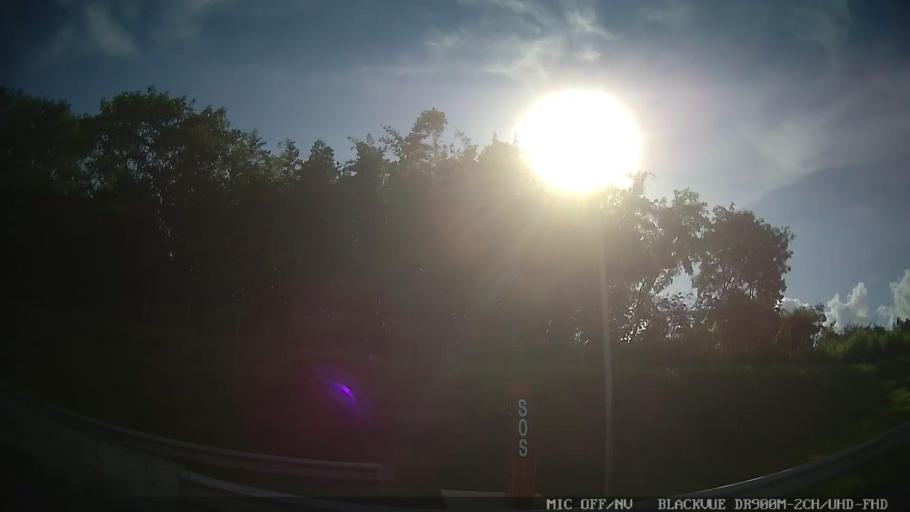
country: BR
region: Sao Paulo
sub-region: Tiete
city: Tiete
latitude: -23.1061
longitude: -47.7642
